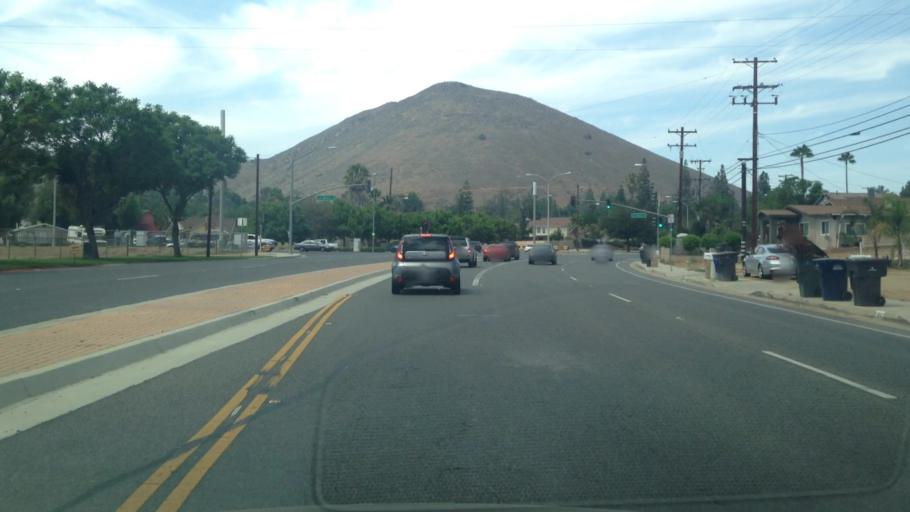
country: US
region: California
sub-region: Riverside County
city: Pedley
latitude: 33.9448
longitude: -117.5004
